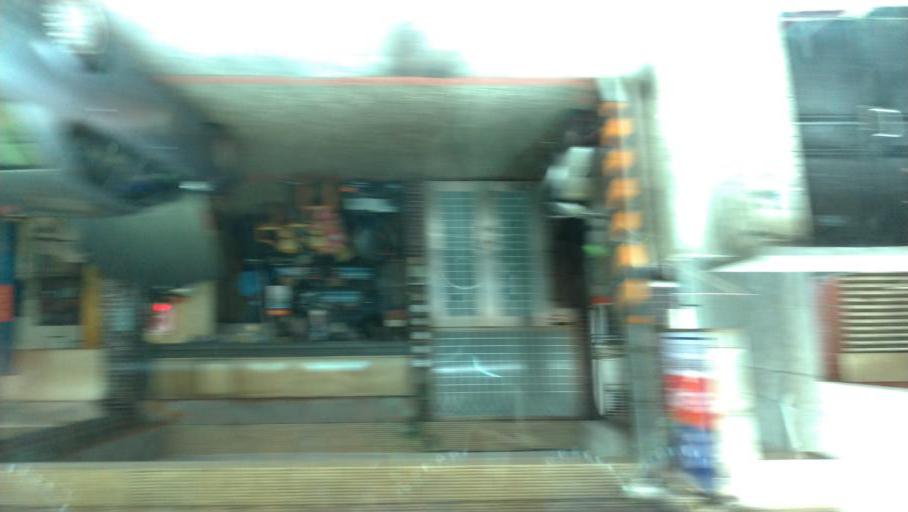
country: TW
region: Taiwan
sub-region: Keelung
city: Keelung
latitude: 25.1478
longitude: 121.7618
